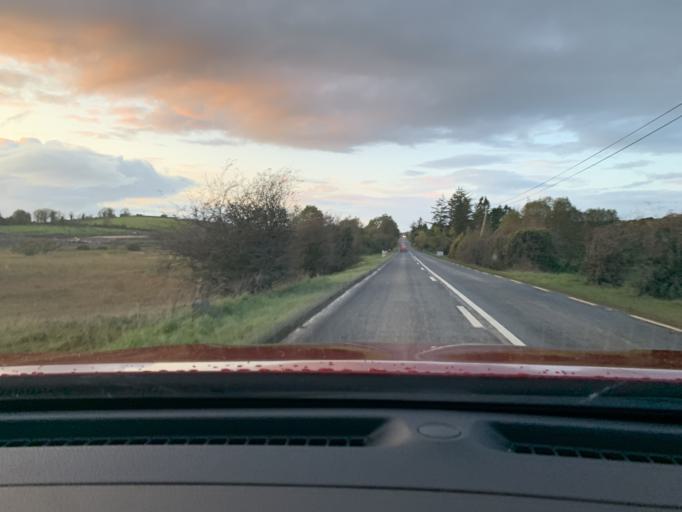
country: IE
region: Connaught
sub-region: Sligo
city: Collooney
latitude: 54.1472
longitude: -8.4615
